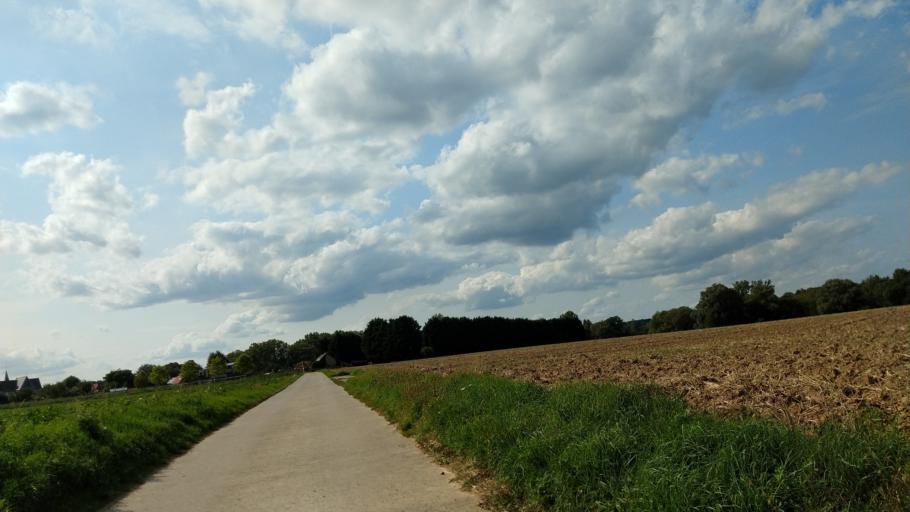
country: BE
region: Flanders
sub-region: Provincie Vlaams-Brabant
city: Boutersem
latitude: 50.8311
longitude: 4.8430
